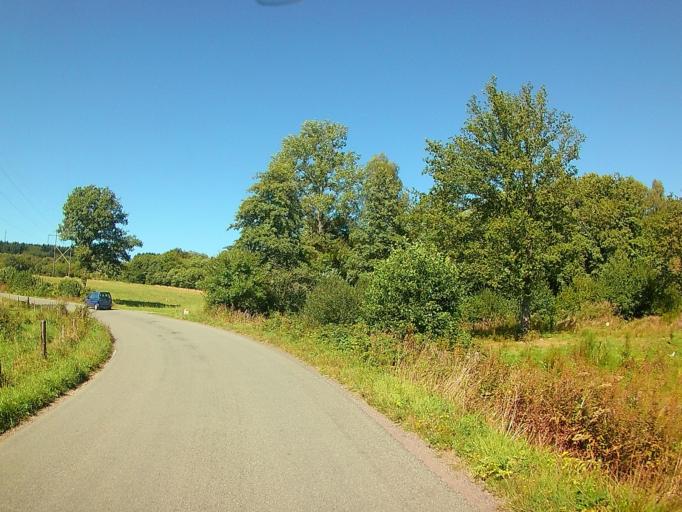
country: FR
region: Auvergne
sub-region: Departement du Puy-de-Dome
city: Manzat
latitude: 45.9179
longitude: 2.9425
